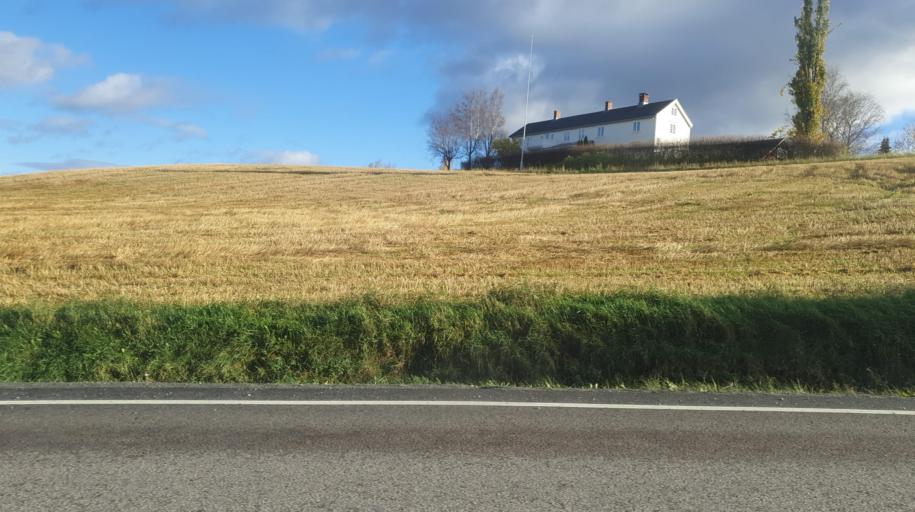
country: NO
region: Sor-Trondelag
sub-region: Klaebu
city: Klaebu
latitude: 63.3067
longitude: 10.4603
